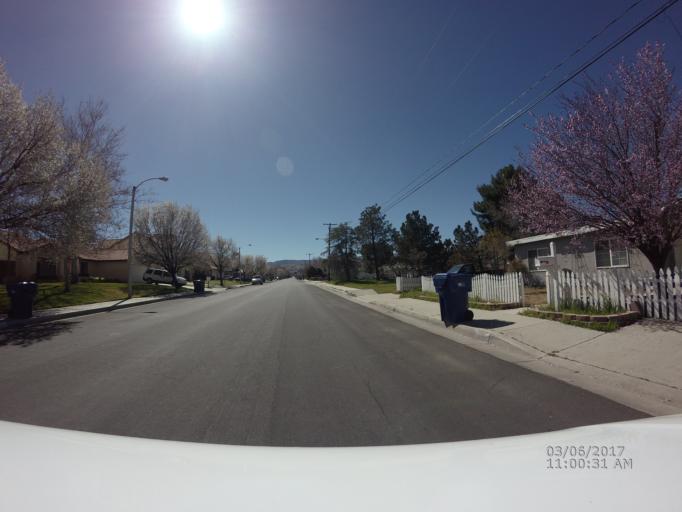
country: US
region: California
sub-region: Los Angeles County
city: Quartz Hill
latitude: 34.6553
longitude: -118.2231
